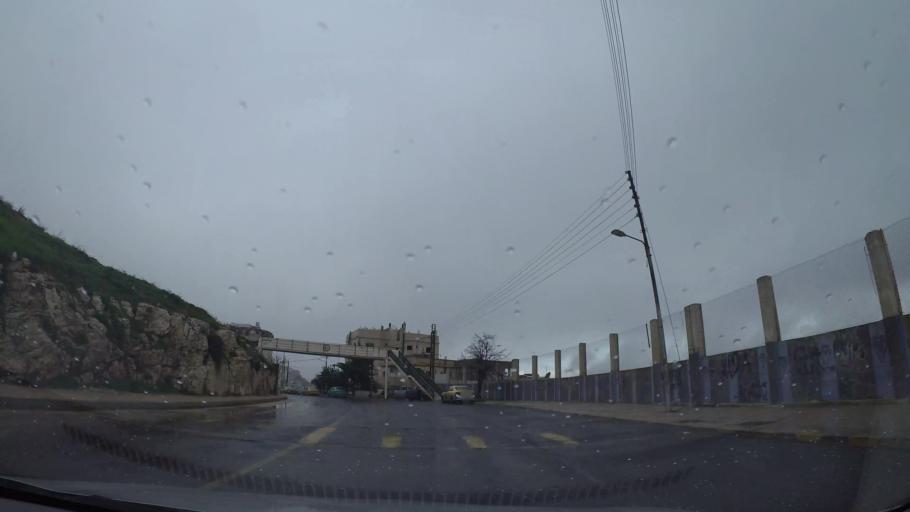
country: JO
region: Amman
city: Al Jubayhah
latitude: 32.0197
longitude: 35.8411
